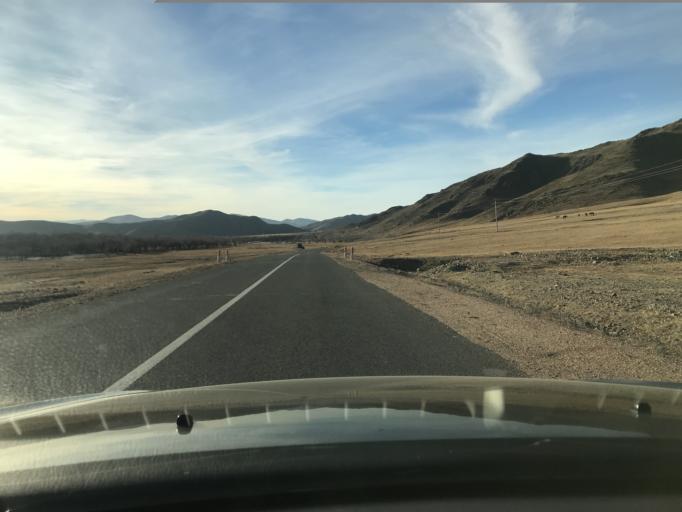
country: MN
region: Central Aimak
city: Dzuunmod
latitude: 47.8218
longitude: 107.3606
